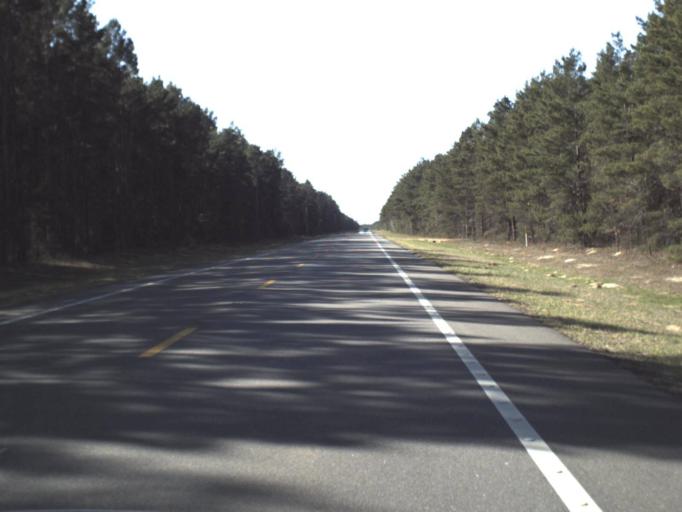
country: US
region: Florida
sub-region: Bay County
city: Youngstown
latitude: 30.4268
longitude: -85.3198
